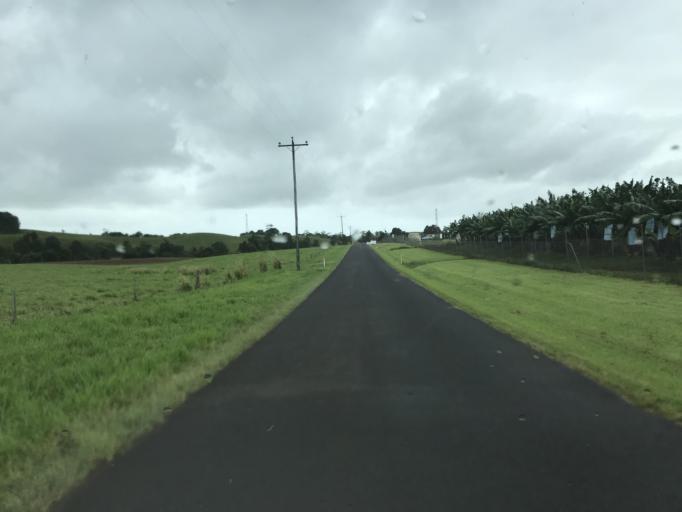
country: AU
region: Queensland
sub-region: Cassowary Coast
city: Innisfail
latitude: -17.5187
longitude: 145.9636
